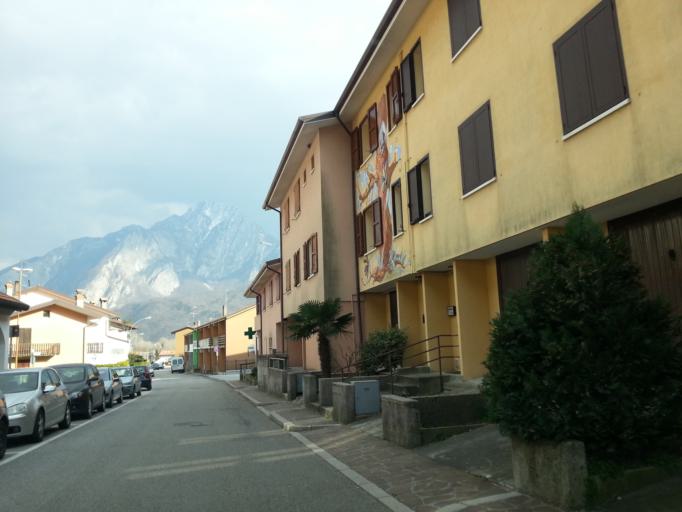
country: IT
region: Friuli Venezia Giulia
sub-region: Provincia di Udine
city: Bordano
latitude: 46.3158
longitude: 13.1029
